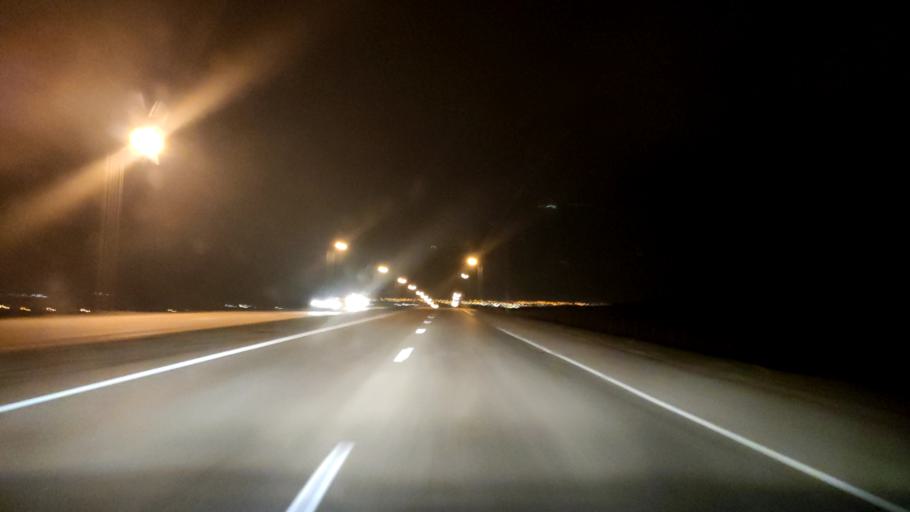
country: RU
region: Belgorod
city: Staryy Oskol
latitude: 51.3386
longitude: 37.7756
